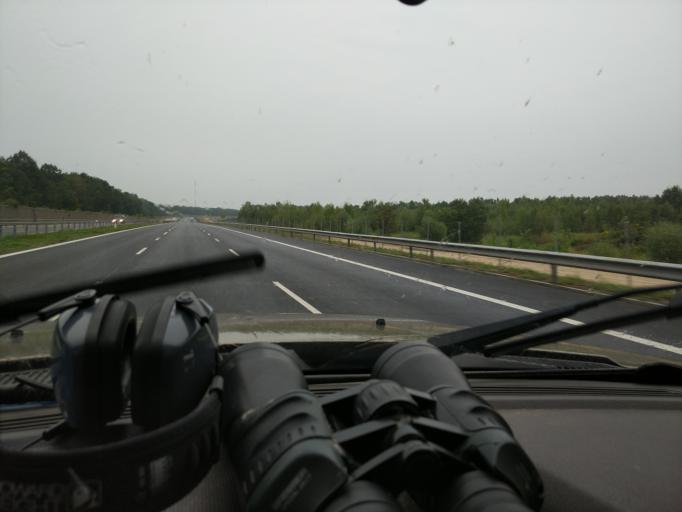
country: PL
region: Masovian Voivodeship
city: Zielonka
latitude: 52.3368
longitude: 21.1569
